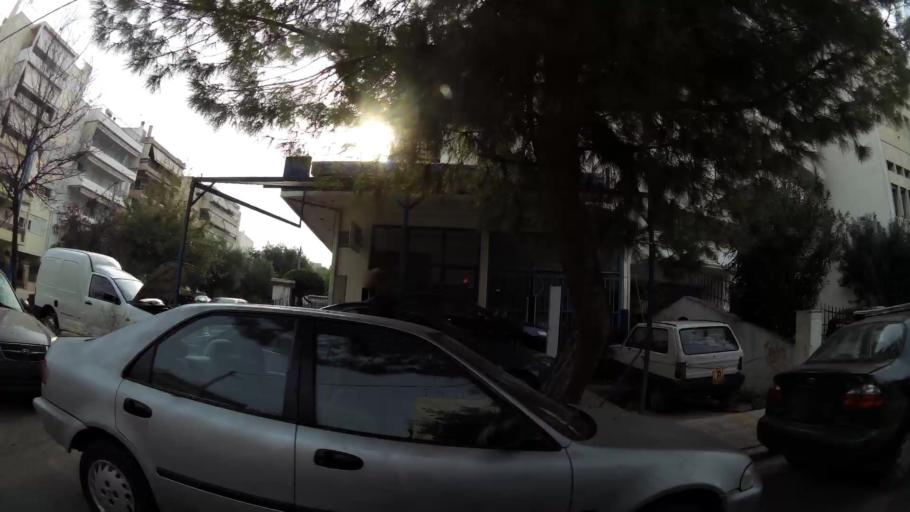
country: GR
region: Attica
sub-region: Nomarchia Athinas
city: Kallithea
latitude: 37.9463
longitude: 23.6934
